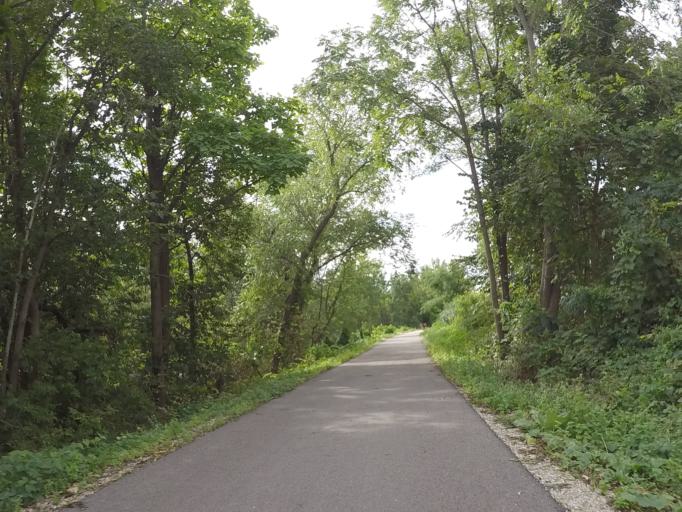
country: US
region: Wisconsin
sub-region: Sauk County
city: Prairie du Sac
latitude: 43.2864
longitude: -89.7179
